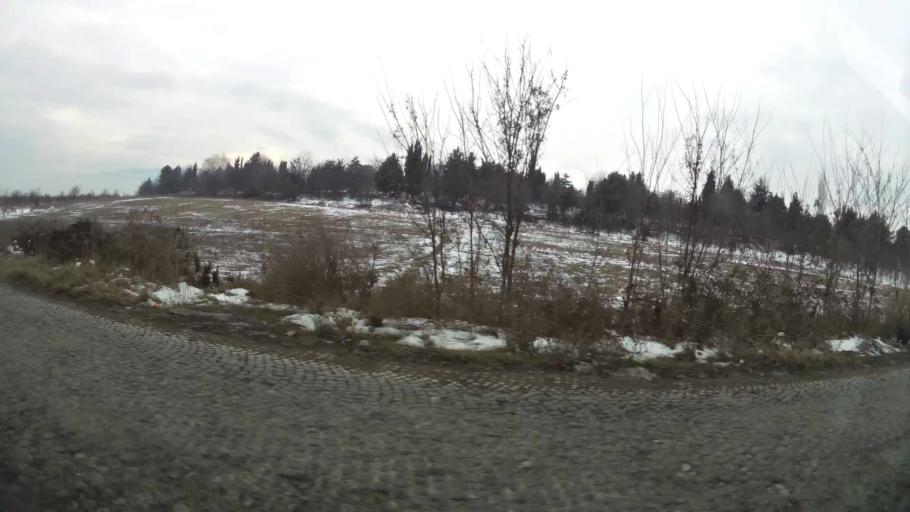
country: MK
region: Butel
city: Butel
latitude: 42.0414
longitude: 21.4384
